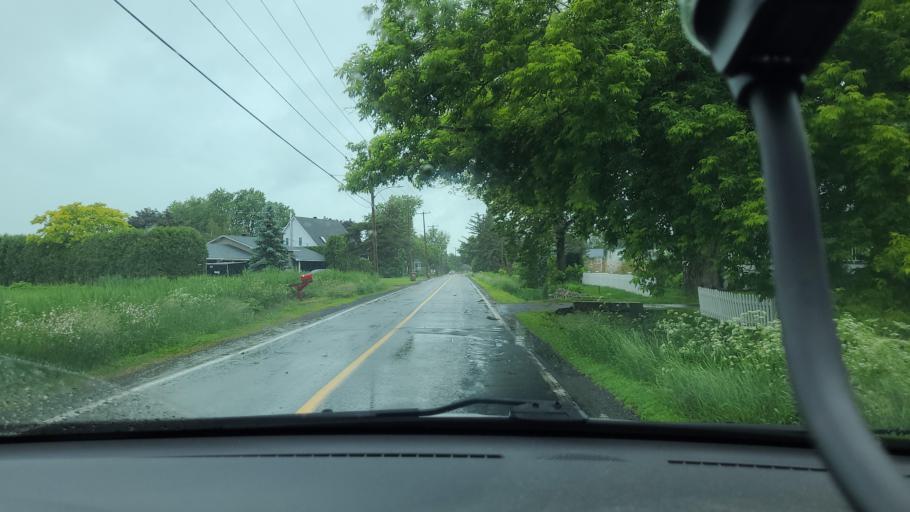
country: CA
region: Quebec
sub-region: Monteregie
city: Saint-Basile-le-Grand
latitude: 45.5533
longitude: -73.2681
